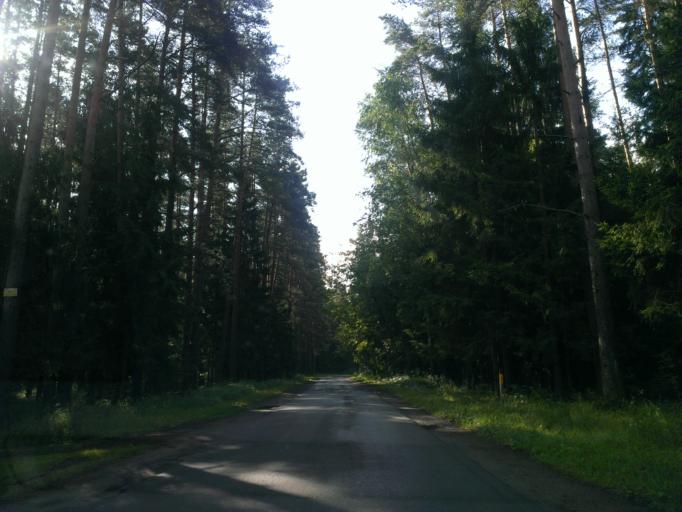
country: LV
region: Incukalns
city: Vangazi
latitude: 57.0990
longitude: 24.5321
